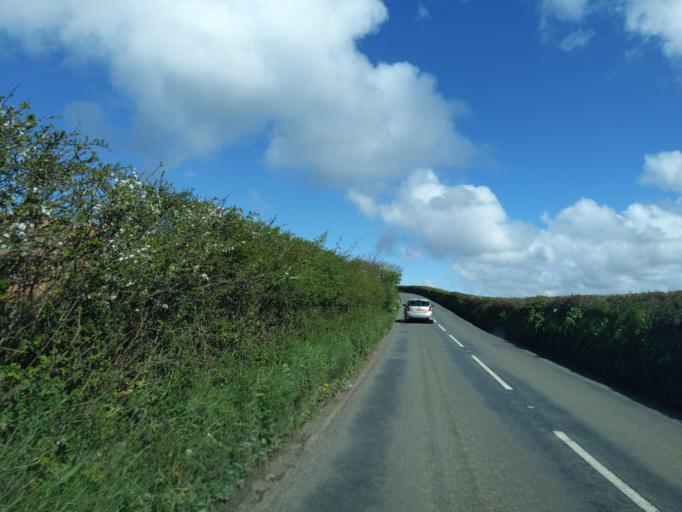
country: GB
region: England
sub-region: Cornwall
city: Wadebridge
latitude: 50.5764
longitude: -4.8095
